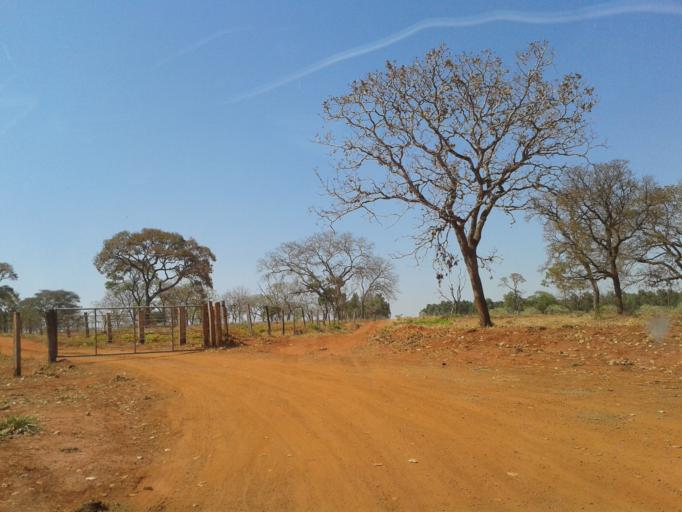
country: BR
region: Minas Gerais
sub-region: Ituiutaba
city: Ituiutaba
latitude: -19.0525
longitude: -49.3771
